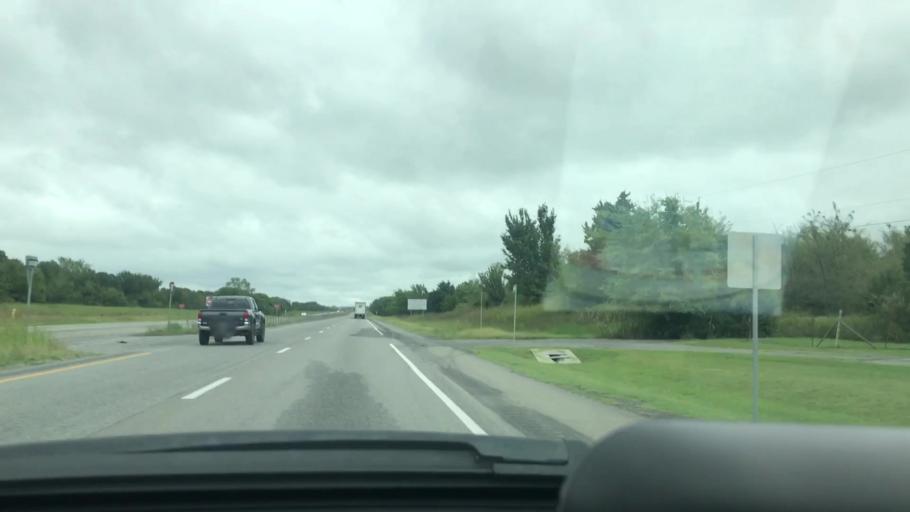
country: US
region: Oklahoma
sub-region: Pittsburg County
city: McAlester
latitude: 34.8018
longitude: -95.8665
